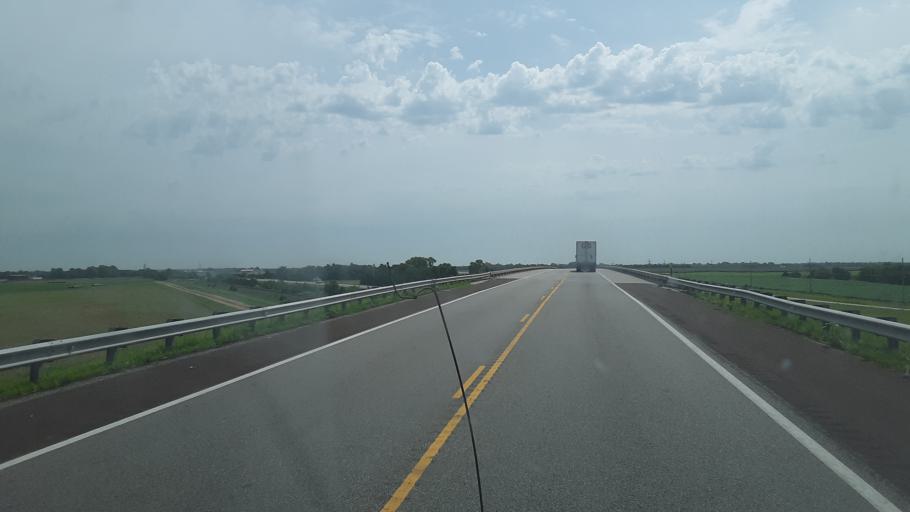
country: US
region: Kansas
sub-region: Reno County
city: South Hutchinson
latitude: 37.9845
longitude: -98.0581
